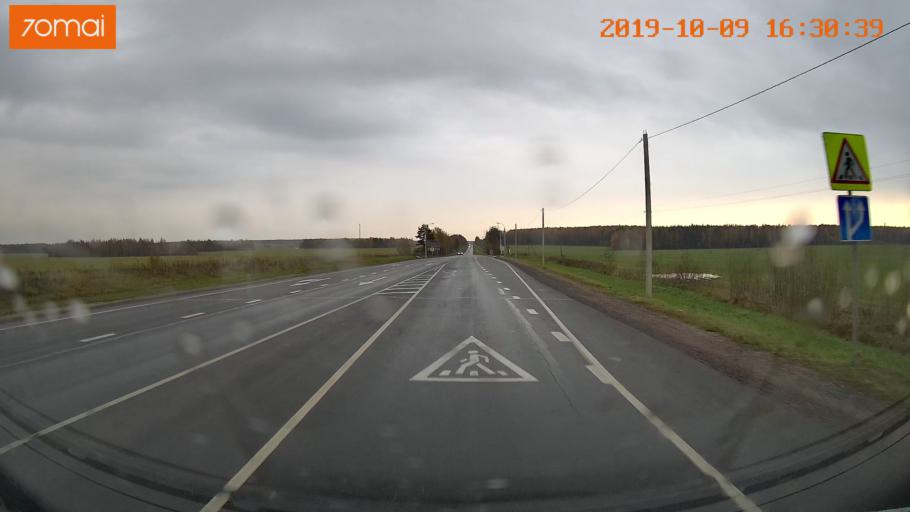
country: RU
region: Kostroma
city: Oktyabr'skiy
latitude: 57.6166
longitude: 40.9425
